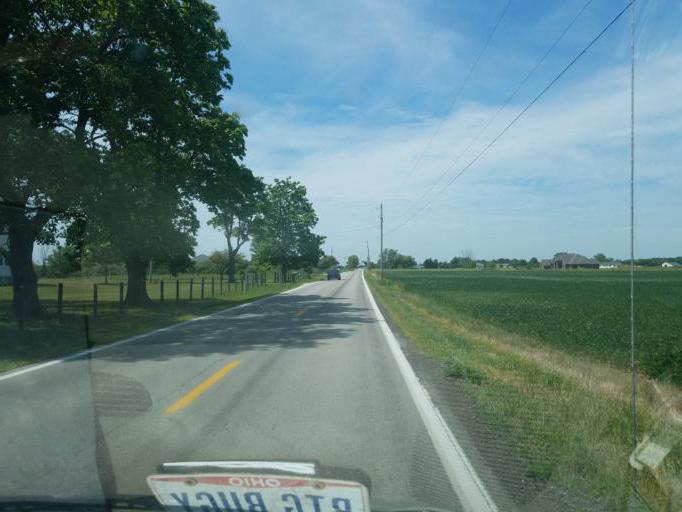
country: US
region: Ohio
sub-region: Madison County
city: West Jefferson
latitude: 39.8665
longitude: -83.2726
